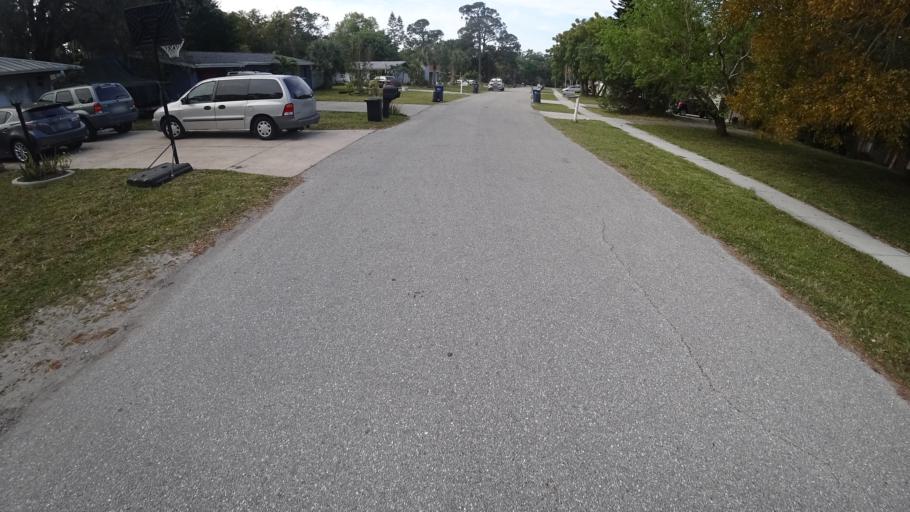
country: US
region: Florida
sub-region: Manatee County
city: Whitfield
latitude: 27.4220
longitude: -82.5513
